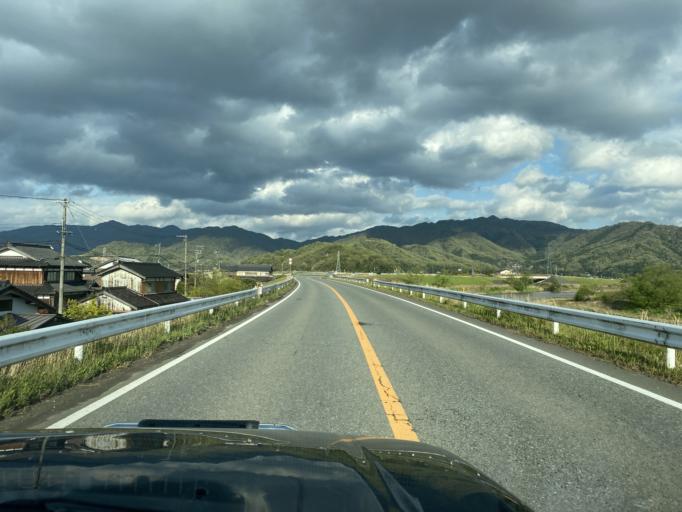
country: JP
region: Hyogo
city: Toyooka
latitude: 35.4888
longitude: 134.8514
